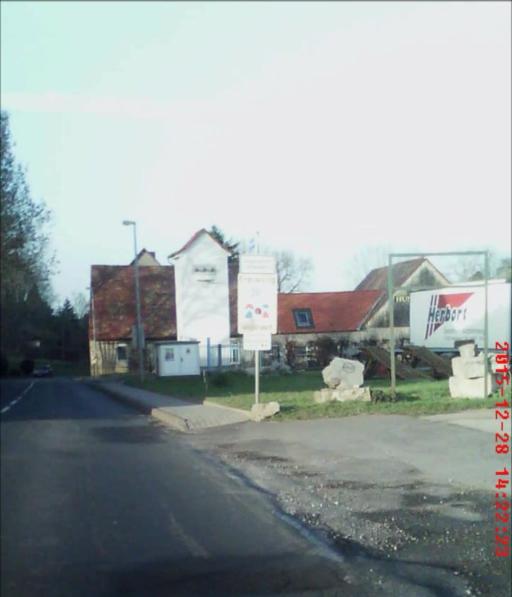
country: DE
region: Thuringia
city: Niederrossla
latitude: 51.0493
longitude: 11.4679
